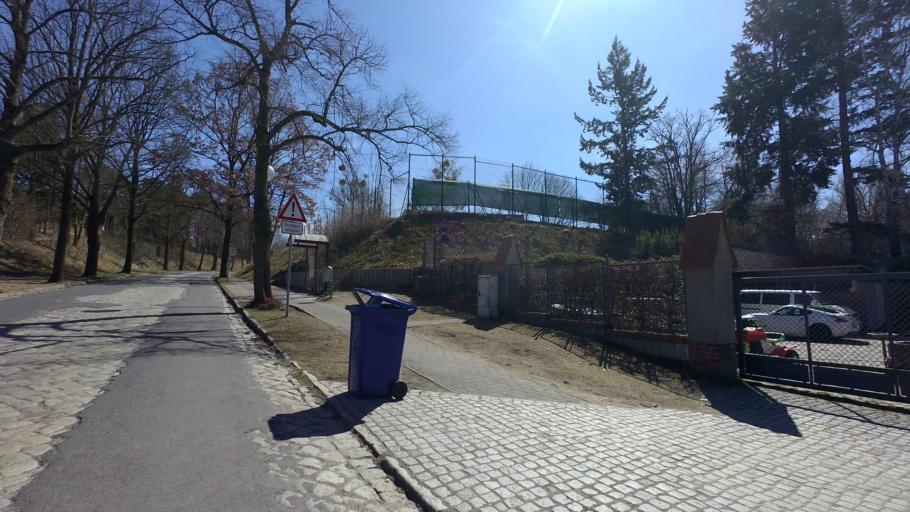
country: DE
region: Brandenburg
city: Teupitz
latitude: 52.1345
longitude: 13.6151
